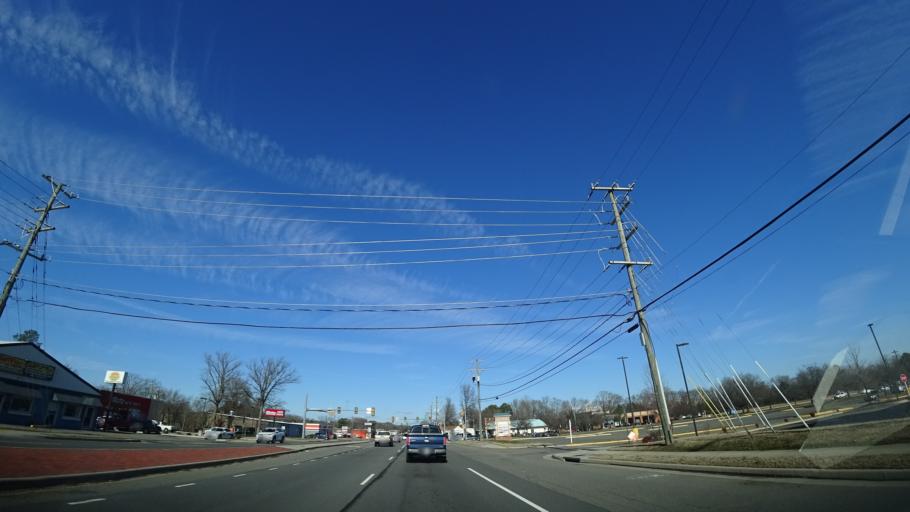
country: US
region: Virginia
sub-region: Hanover County
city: Ashland
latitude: 37.7545
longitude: -77.4714
